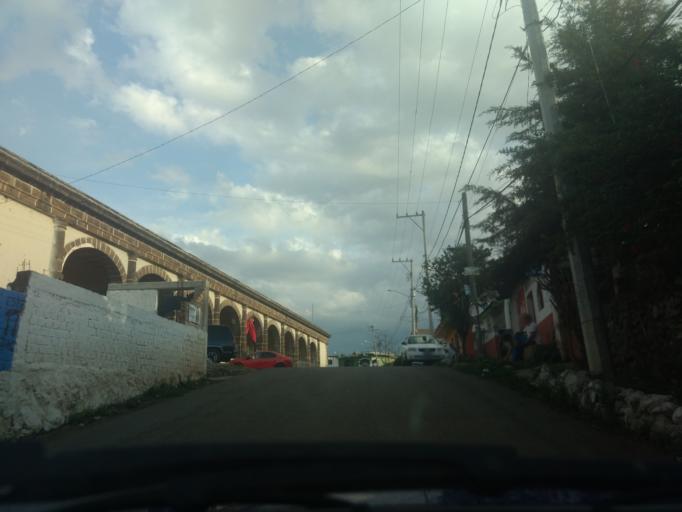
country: MX
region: Nayarit
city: Puga
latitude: 21.5274
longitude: -104.8075
